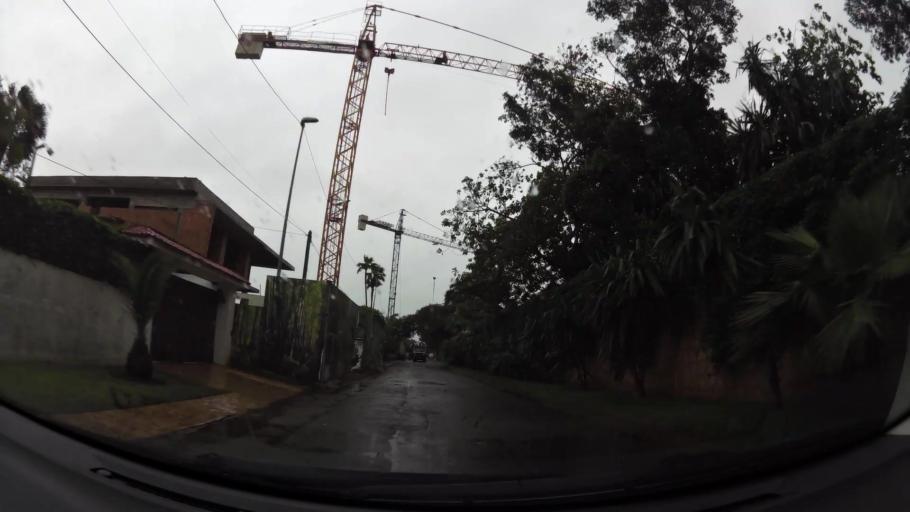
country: MA
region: Grand Casablanca
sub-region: Casablanca
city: Casablanca
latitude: 33.5883
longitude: -7.6688
